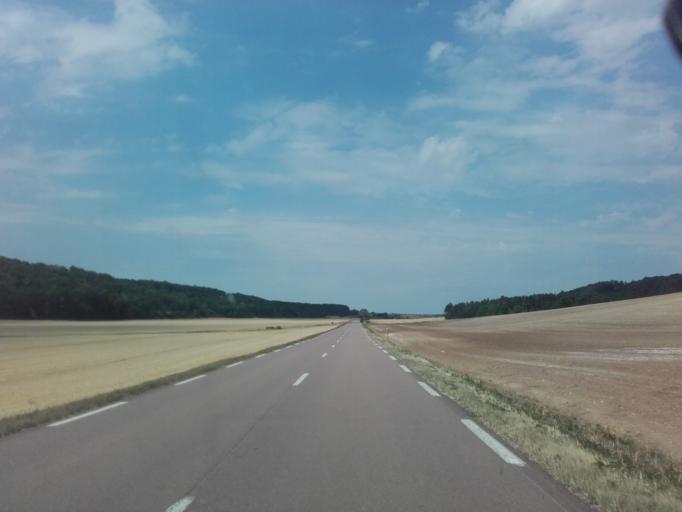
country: FR
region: Bourgogne
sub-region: Departement de l'Yonne
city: Chablis
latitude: 47.7701
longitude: 3.8138
